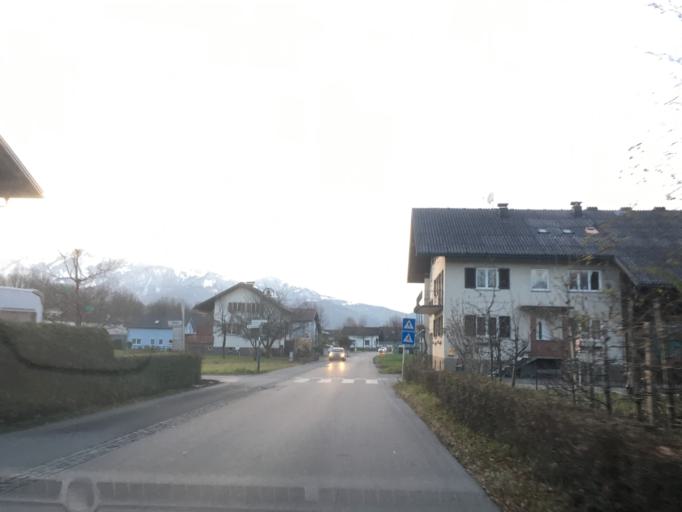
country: AT
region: Vorarlberg
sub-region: Politischer Bezirk Feldkirch
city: Koblach
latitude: 47.3122
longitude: 9.6123
